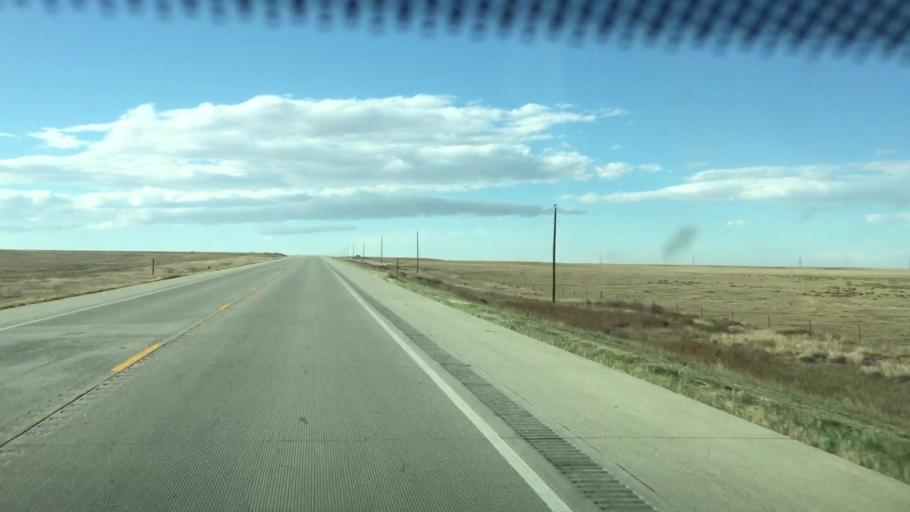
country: US
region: Colorado
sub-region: Lincoln County
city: Hugo
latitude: 39.0716
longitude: -103.3760
